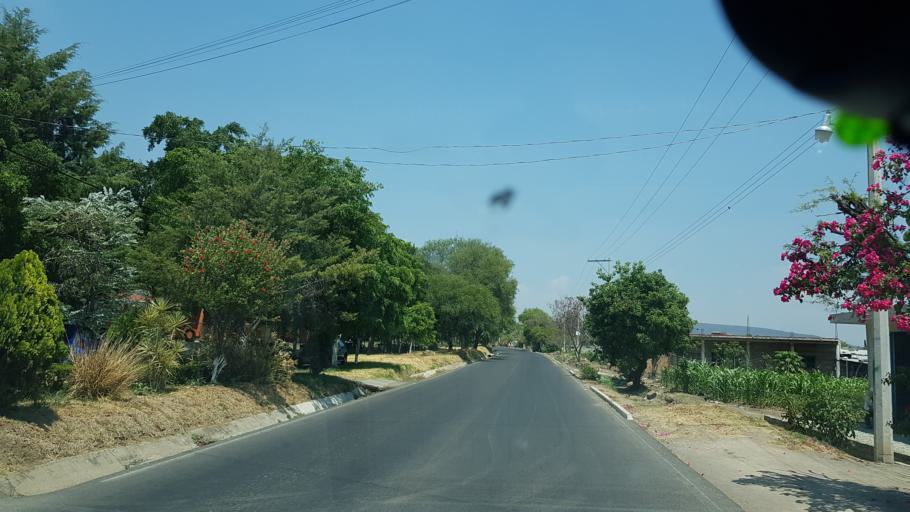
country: MX
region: Puebla
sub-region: Huaquechula
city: Cacaloxuchitl
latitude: 18.7882
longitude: -98.4783
